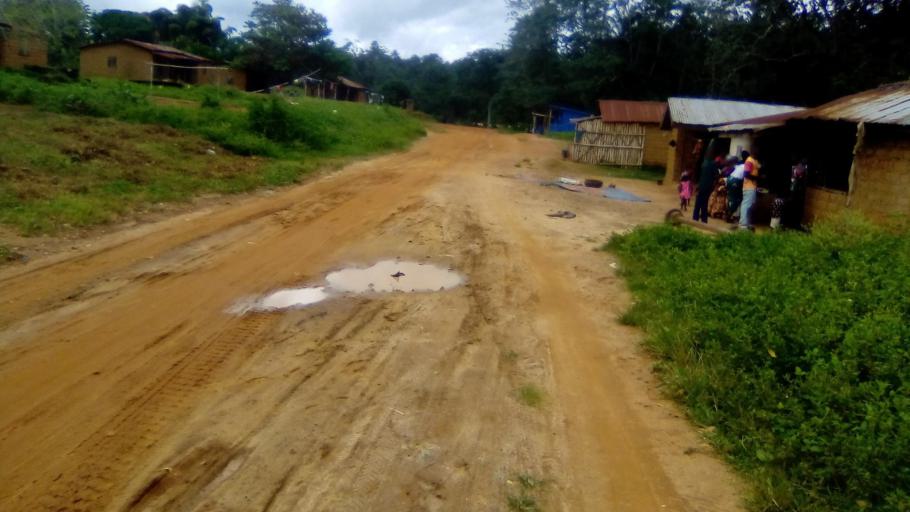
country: SL
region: Eastern Province
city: Simbakoro
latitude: 8.5509
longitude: -10.9286
